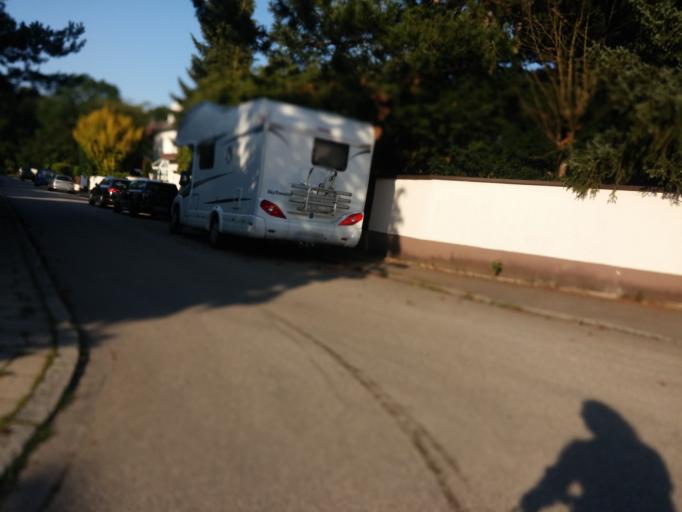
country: DE
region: Bavaria
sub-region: Upper Bavaria
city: Neubiberg
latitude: 48.1058
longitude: 11.6729
